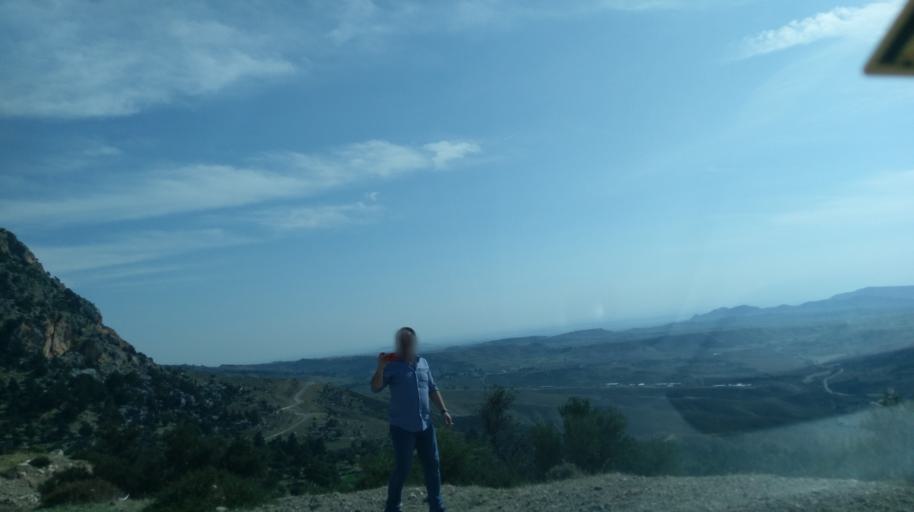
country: CY
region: Keryneia
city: Lapithos
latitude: 35.3213
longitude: 33.1202
